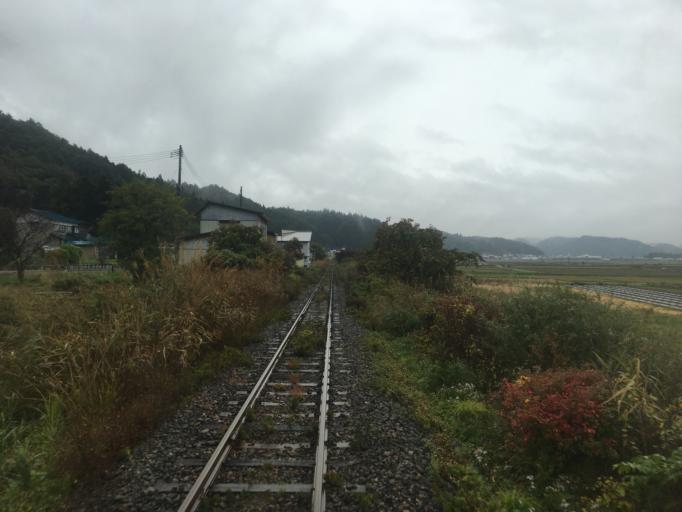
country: JP
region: Yamagata
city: Obanazawa
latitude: 38.7647
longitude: 140.4935
